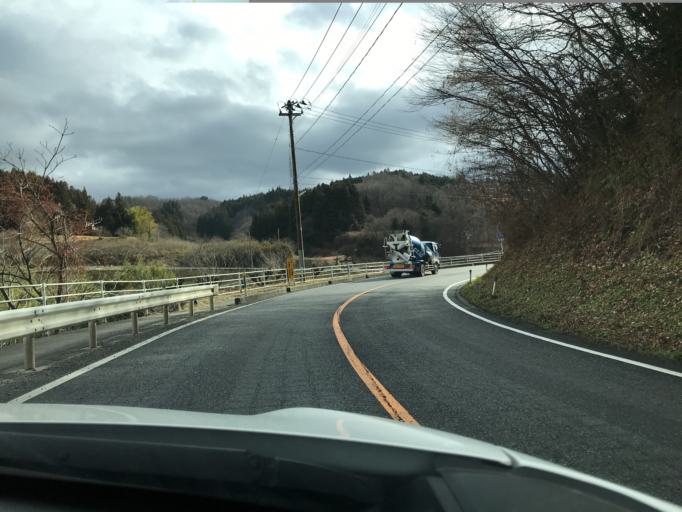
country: JP
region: Fukushima
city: Funehikimachi-funehiki
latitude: 37.5768
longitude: 140.5789
